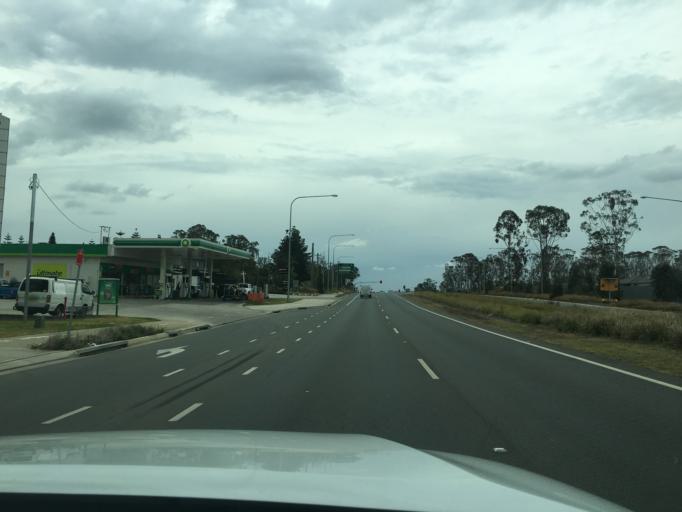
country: AU
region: New South Wales
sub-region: Campbelltown Municipality
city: Denham Court
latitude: -33.9715
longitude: 150.8127
